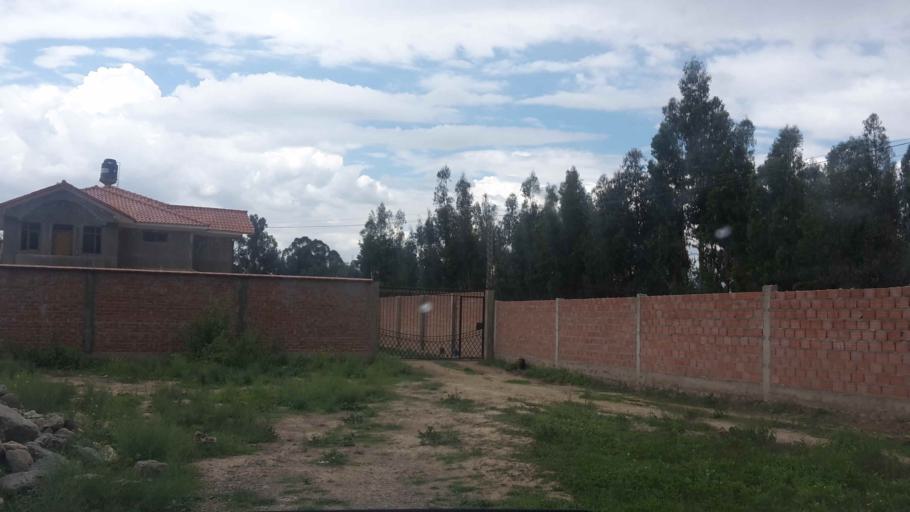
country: BO
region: Cochabamba
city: Cochabamba
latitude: -17.3386
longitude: -66.2265
